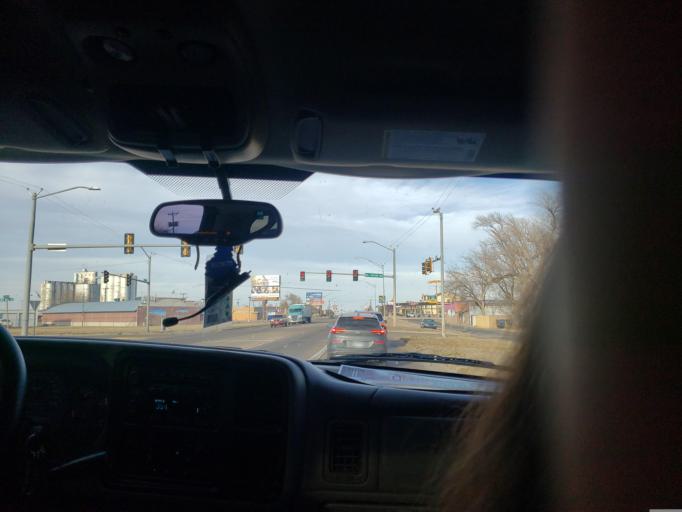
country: US
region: Oklahoma
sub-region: Texas County
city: Guymon
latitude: 36.6807
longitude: -101.4715
